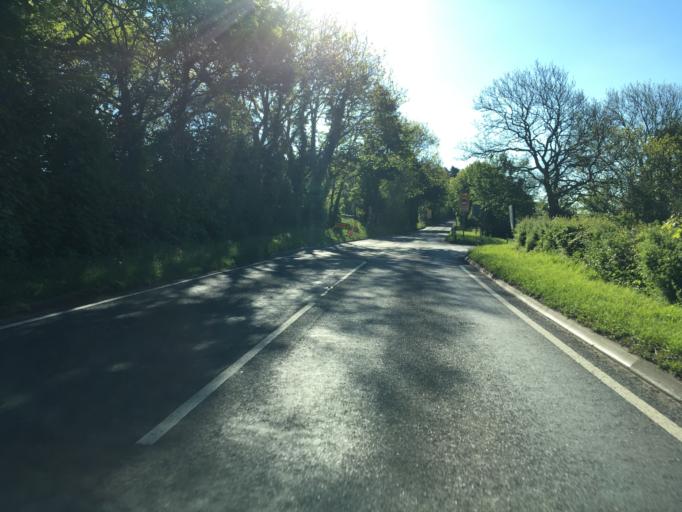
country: GB
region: England
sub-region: North Somerset
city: Nailsea
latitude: 51.4508
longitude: -2.7325
